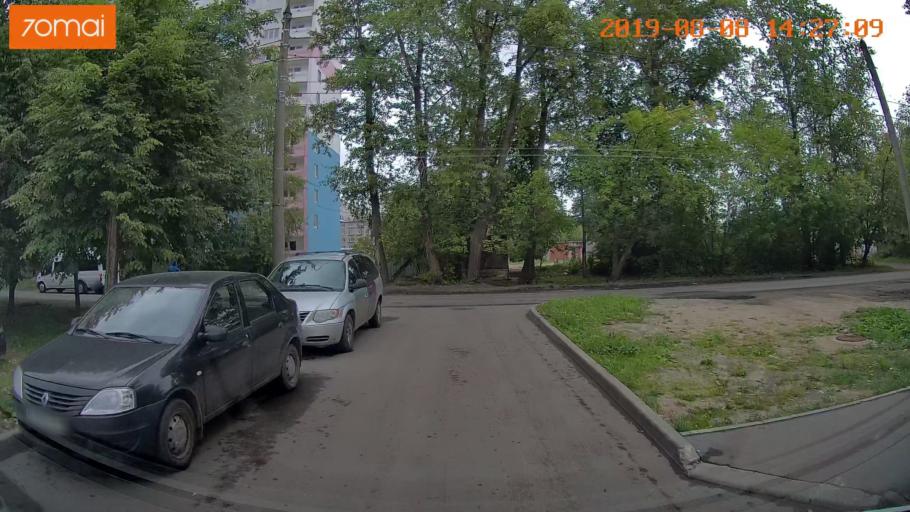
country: RU
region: Ivanovo
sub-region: Gorod Ivanovo
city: Ivanovo
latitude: 56.9982
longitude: 40.9413
